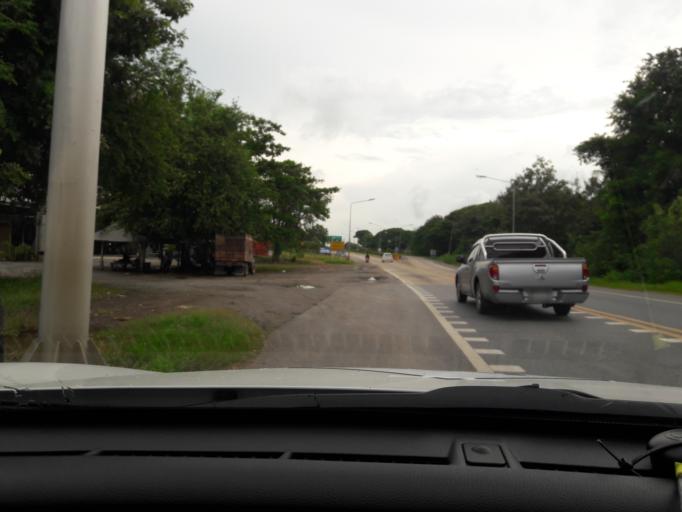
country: TH
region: Nakhon Sawan
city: Tak Fa
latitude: 15.3559
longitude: 100.5025
